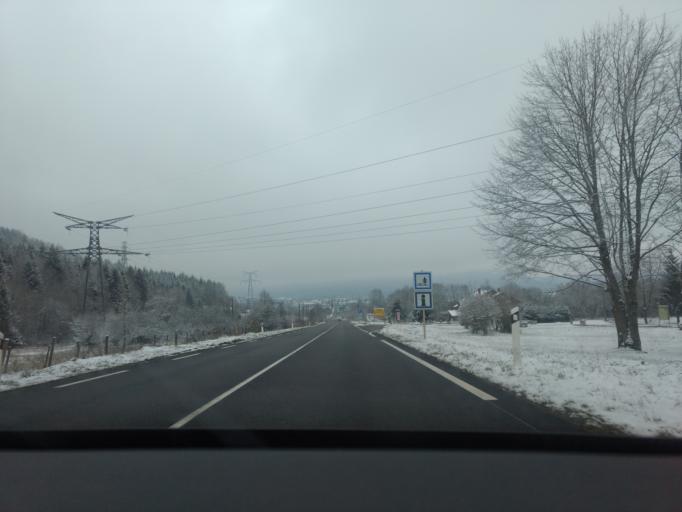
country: FR
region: Franche-Comte
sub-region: Departement du Jura
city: Champagnole
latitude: 46.7680
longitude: 5.9049
